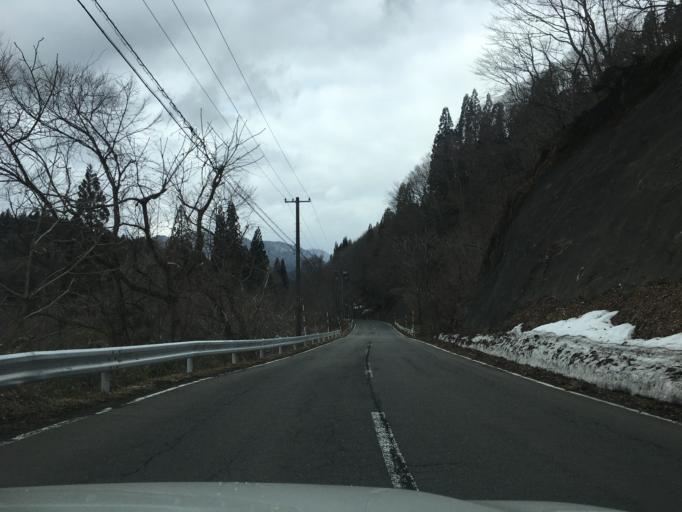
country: JP
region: Akita
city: Odate
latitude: 40.4287
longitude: 140.6469
